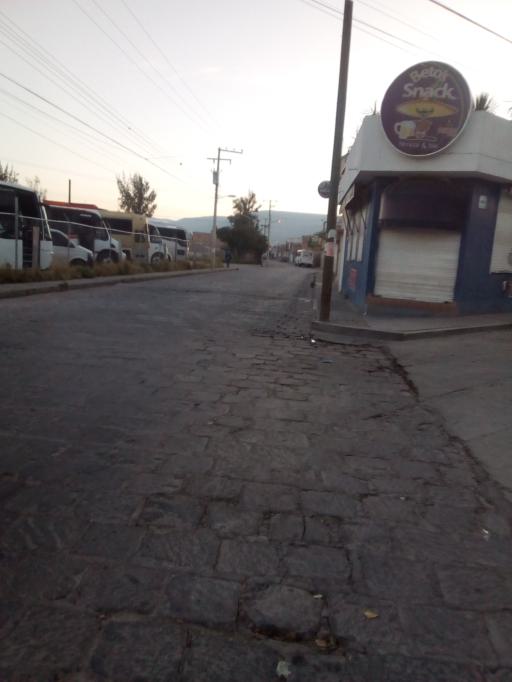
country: MX
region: Guerrero
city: San Luis de la Paz
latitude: 21.2910
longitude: -100.5228
